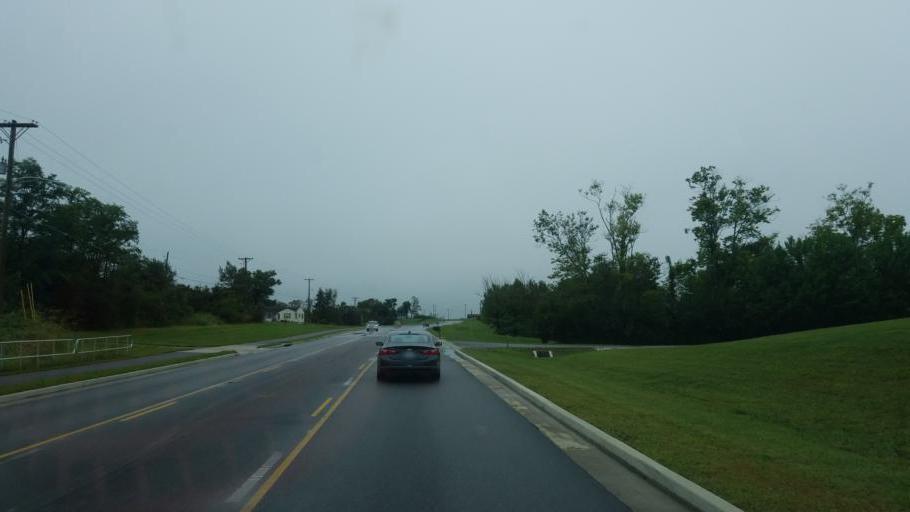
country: US
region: Ohio
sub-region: Brown County
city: Aberdeen
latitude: 38.6309
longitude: -83.7821
